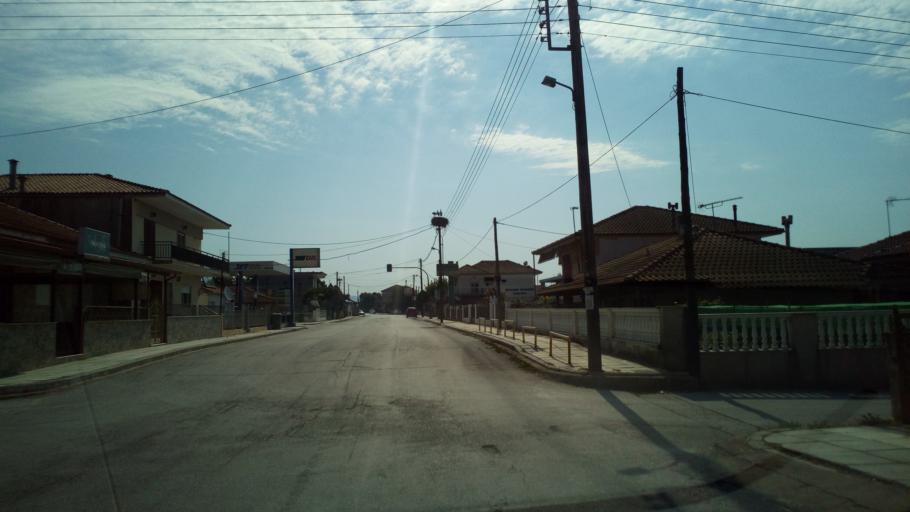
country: GR
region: Central Macedonia
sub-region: Nomos Thessalonikis
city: Askos
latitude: 40.6931
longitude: 23.3272
